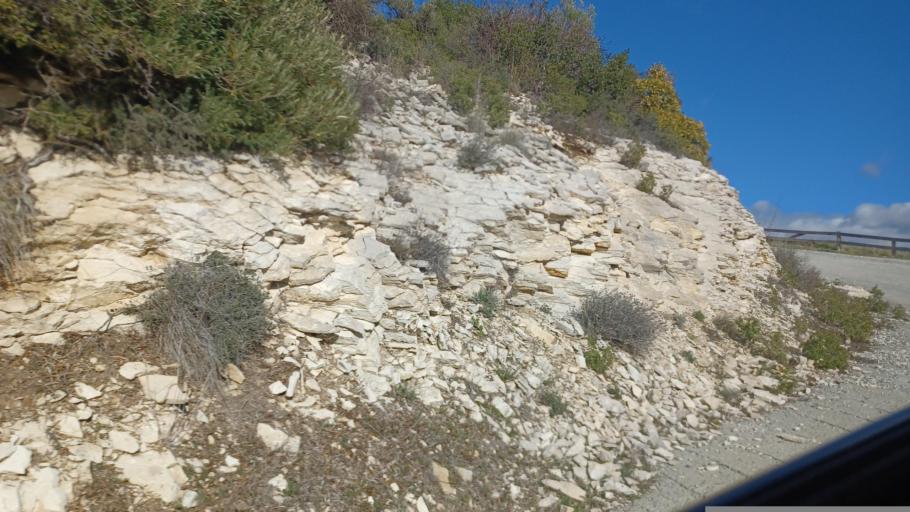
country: CY
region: Limassol
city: Pano Polemidia
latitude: 34.7956
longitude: 32.9914
